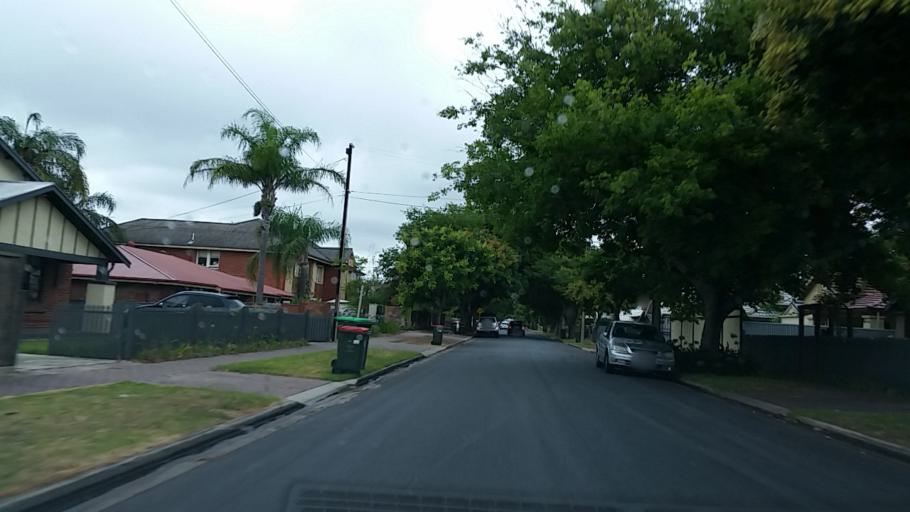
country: AU
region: South Australia
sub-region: Prospect
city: Prospect
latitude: -34.8786
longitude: 138.6036
